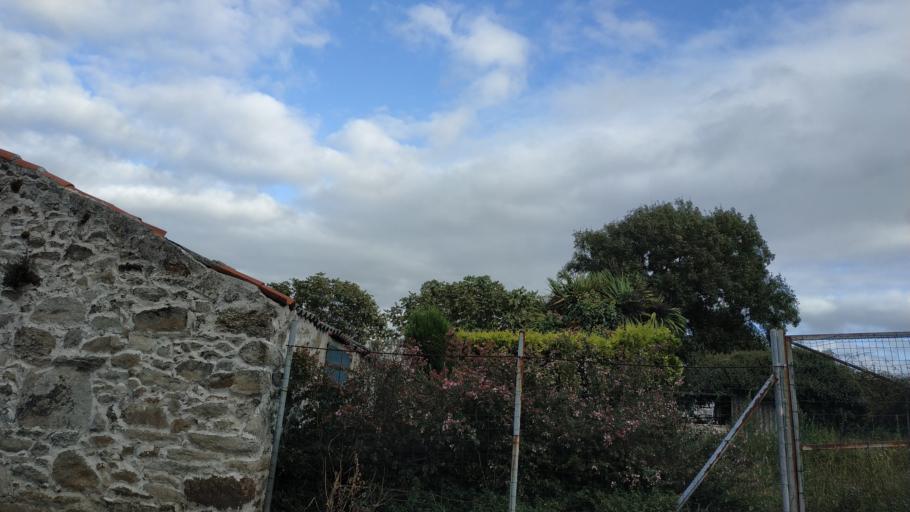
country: ES
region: Galicia
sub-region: Provincia da Coruna
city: A Coruna
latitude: 43.3678
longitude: -8.4297
